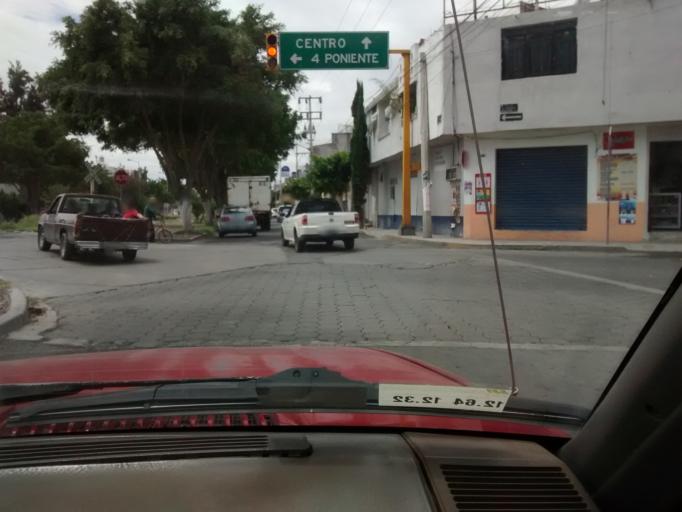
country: MX
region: Puebla
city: Tehuacan
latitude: 18.4676
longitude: -97.4033
